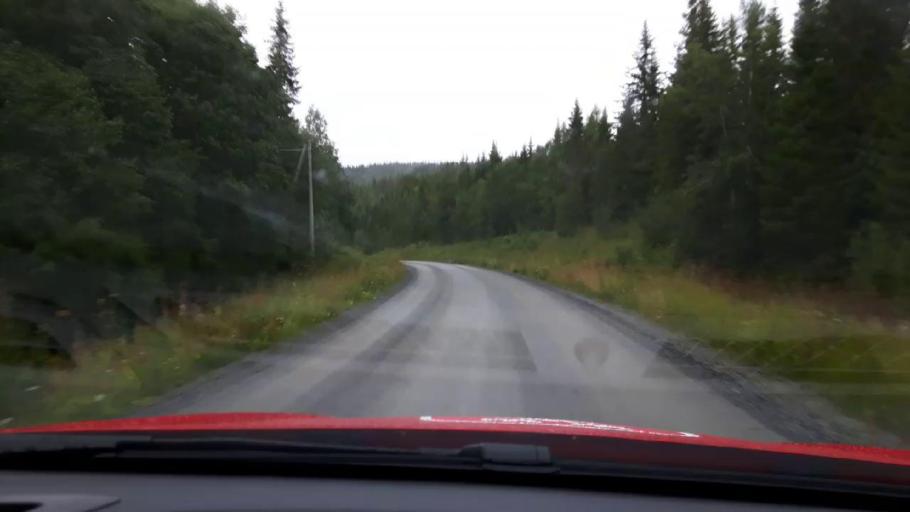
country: SE
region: Jaemtland
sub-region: Are Kommun
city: Are
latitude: 63.4762
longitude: 12.8094
